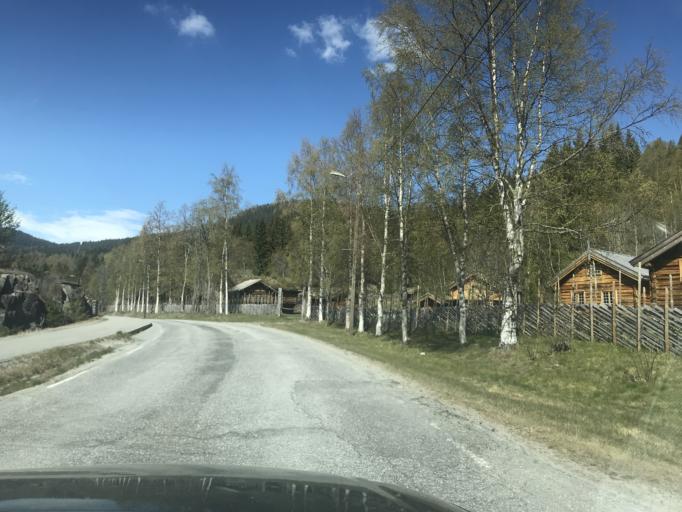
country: NO
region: Telemark
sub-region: Hjartdal
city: Sauland
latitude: 59.7534
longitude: 8.7965
